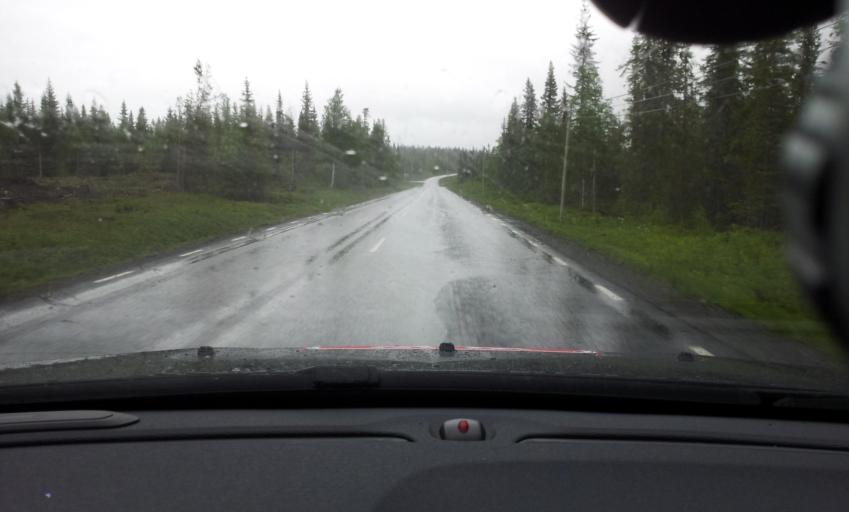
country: SE
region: Jaemtland
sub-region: Are Kommun
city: Are
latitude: 63.2511
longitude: 13.2026
